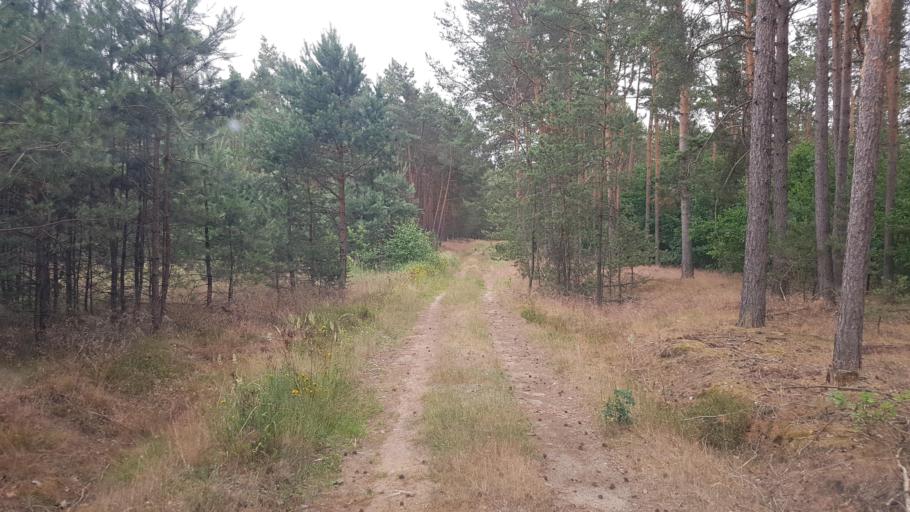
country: DE
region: Brandenburg
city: Treuenbrietzen
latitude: 52.0463
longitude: 12.8190
